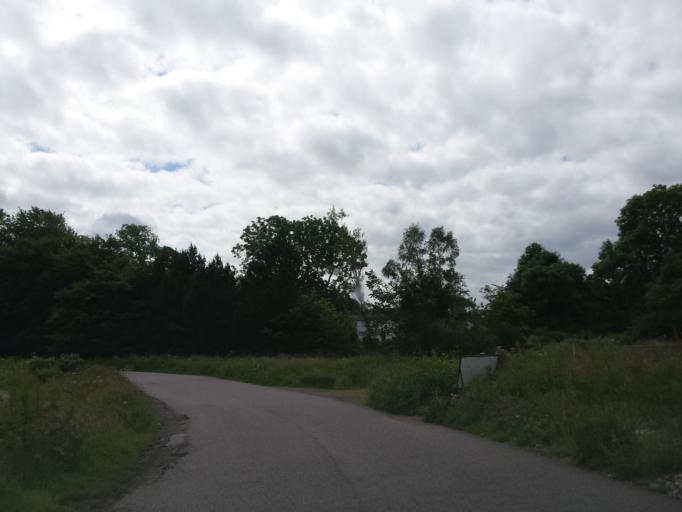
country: GB
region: Scotland
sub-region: Argyll and Bute
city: Oban
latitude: 56.4487
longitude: -5.4455
